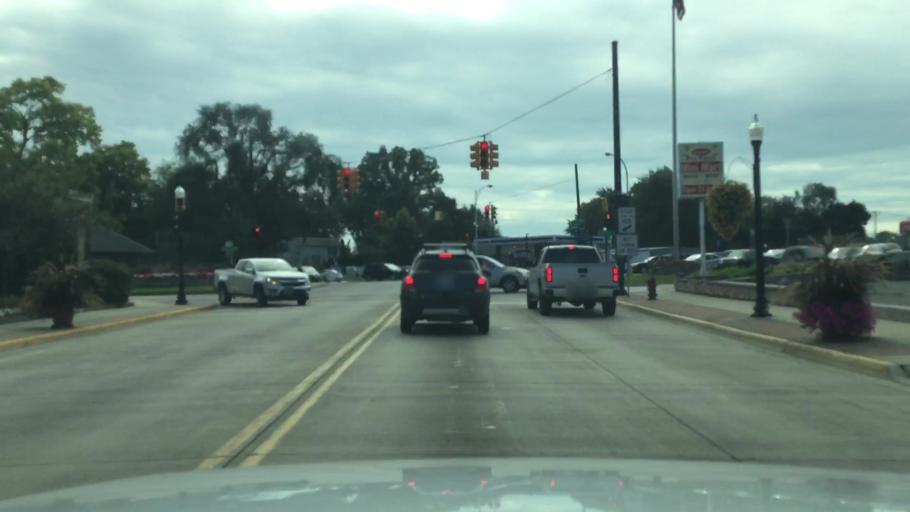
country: US
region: Michigan
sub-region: Wayne County
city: Belleville
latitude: 42.2051
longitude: -83.4859
